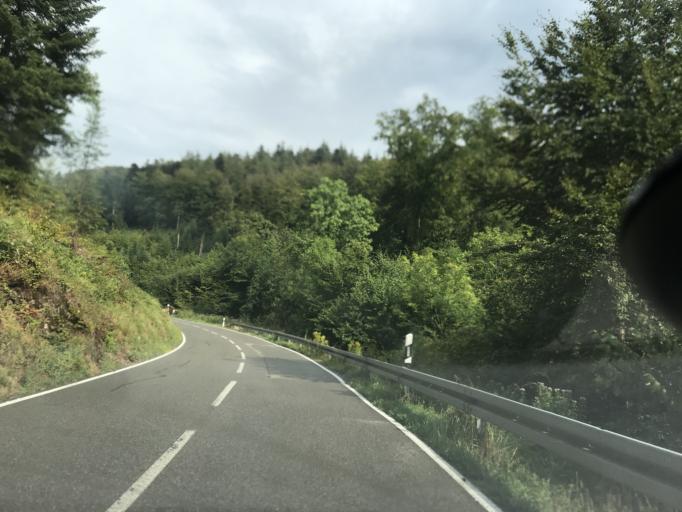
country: DE
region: Baden-Wuerttemberg
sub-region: Freiburg Region
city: Kandern
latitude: 47.7097
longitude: 7.6828
